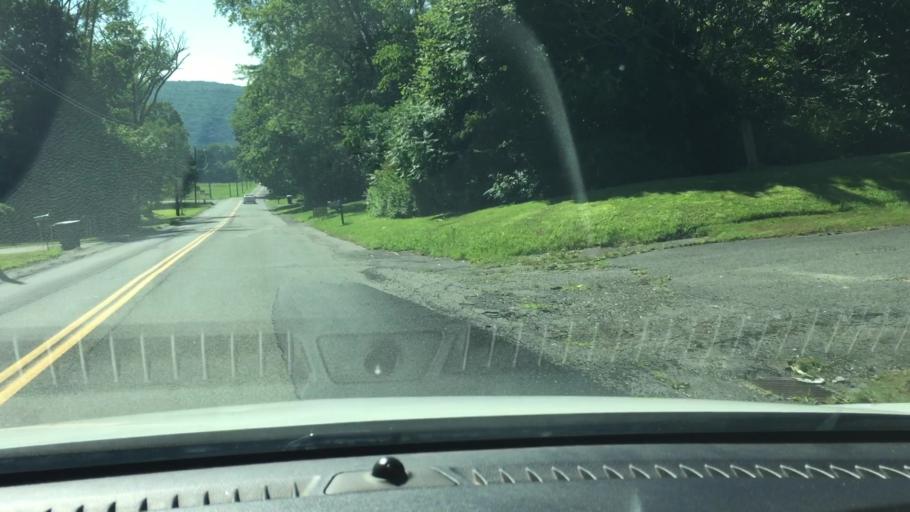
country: US
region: Massachusetts
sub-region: Berkshire County
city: Lanesborough
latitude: 42.5137
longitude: -73.2199
